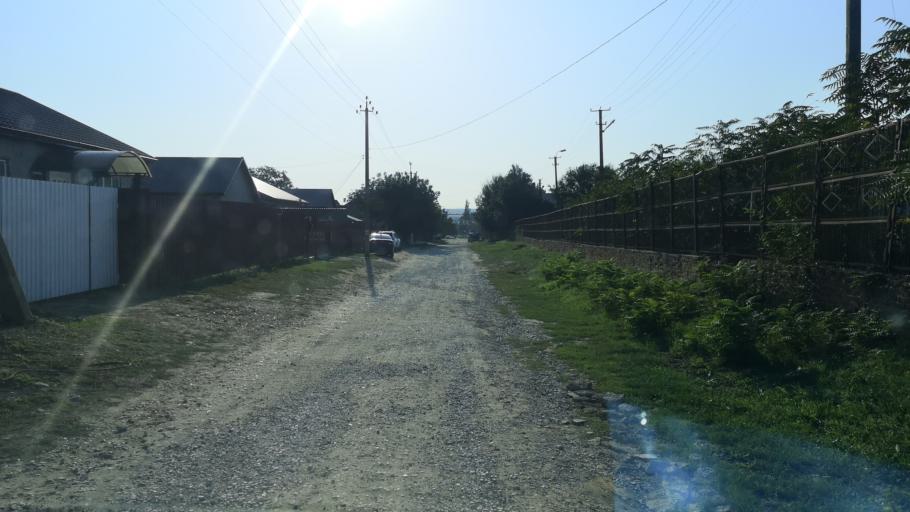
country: RU
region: Krasnodarskiy
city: Taman'
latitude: 45.2099
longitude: 36.6975
